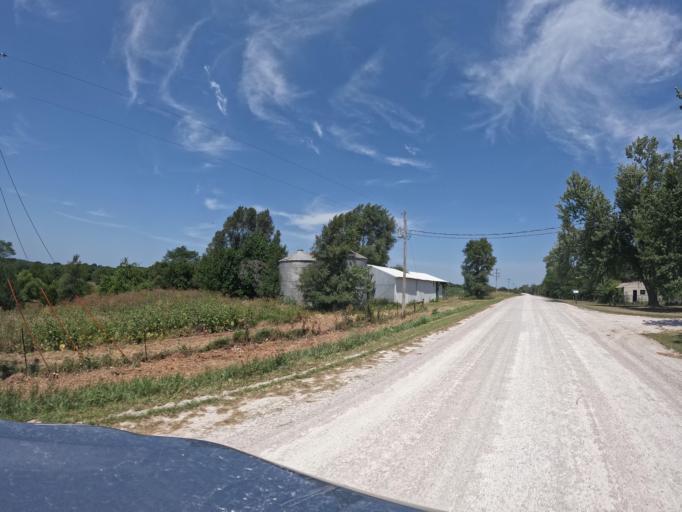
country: US
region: Iowa
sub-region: Henry County
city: Mount Pleasant
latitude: 40.9001
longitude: -91.5361
